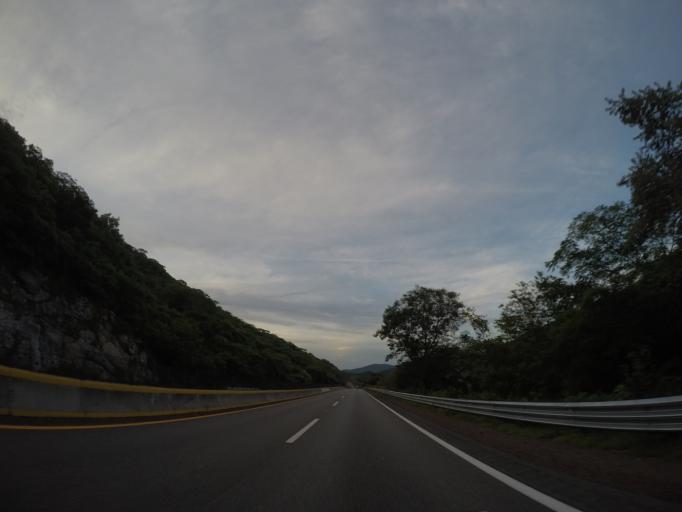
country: MX
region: Guerrero
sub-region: Huitzuco de los Figueroa
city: Ciudad de Huitzuco
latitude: 18.3406
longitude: -99.1898
